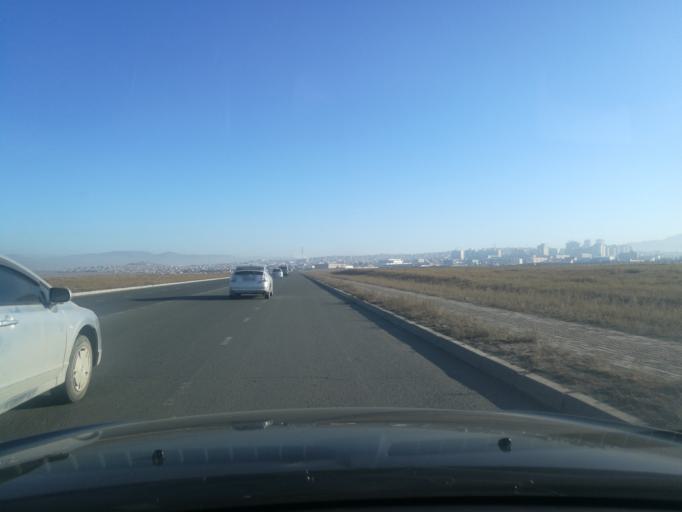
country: MN
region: Ulaanbaatar
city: Ulaanbaatar
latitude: 47.8525
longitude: 106.7438
